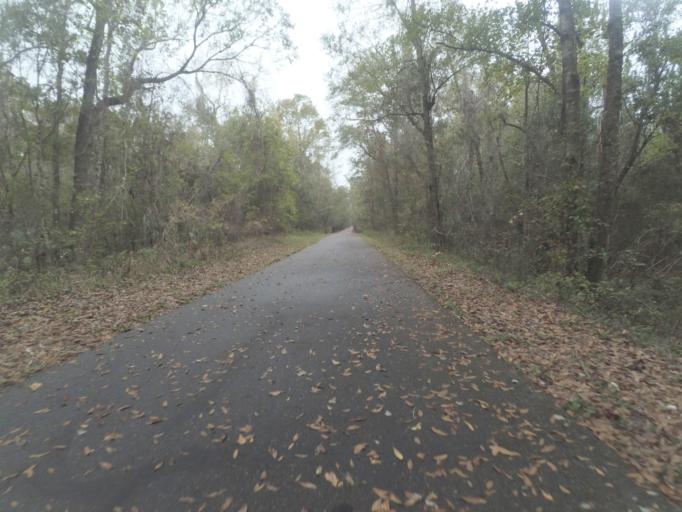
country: US
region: Florida
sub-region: Alachua County
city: Hawthorne
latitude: 29.5970
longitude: -82.1444
